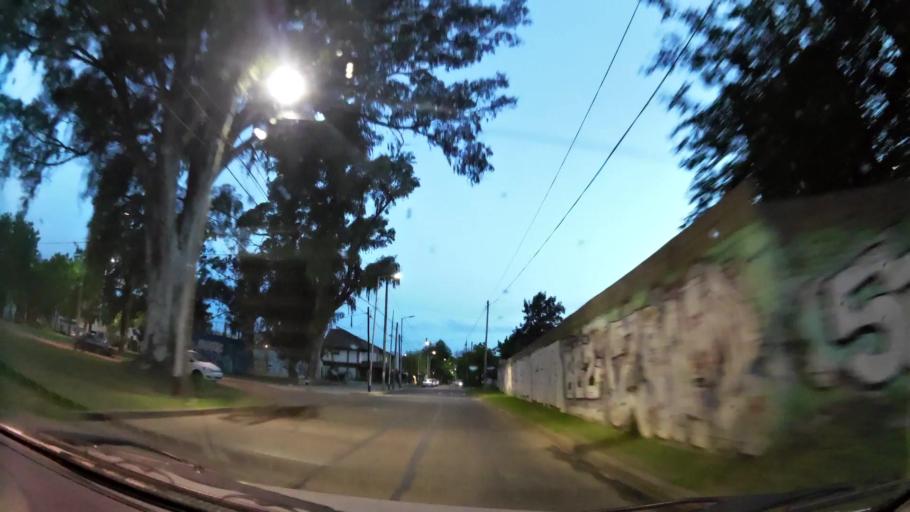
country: AR
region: Buenos Aires
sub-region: Partido de Avellaneda
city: Avellaneda
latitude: -34.6941
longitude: -58.3127
